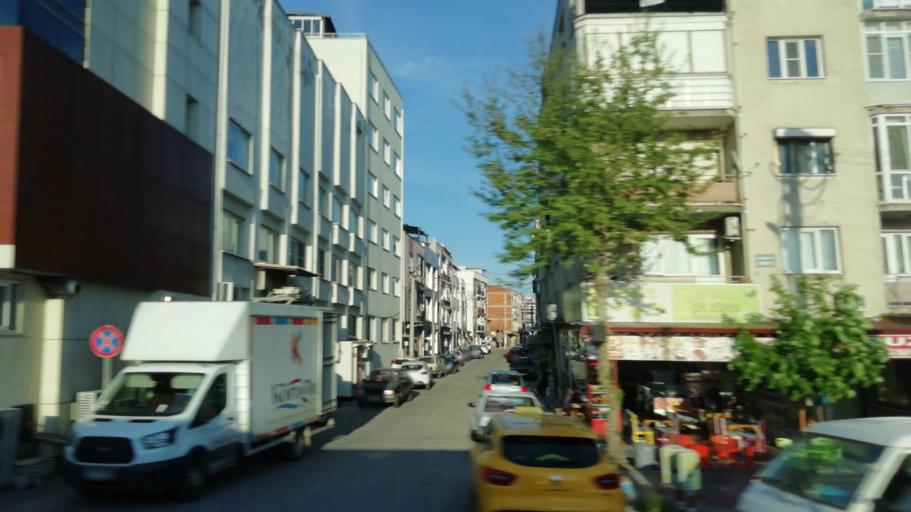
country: TR
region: Manisa
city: Akhisar
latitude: 38.9282
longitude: 27.8343
